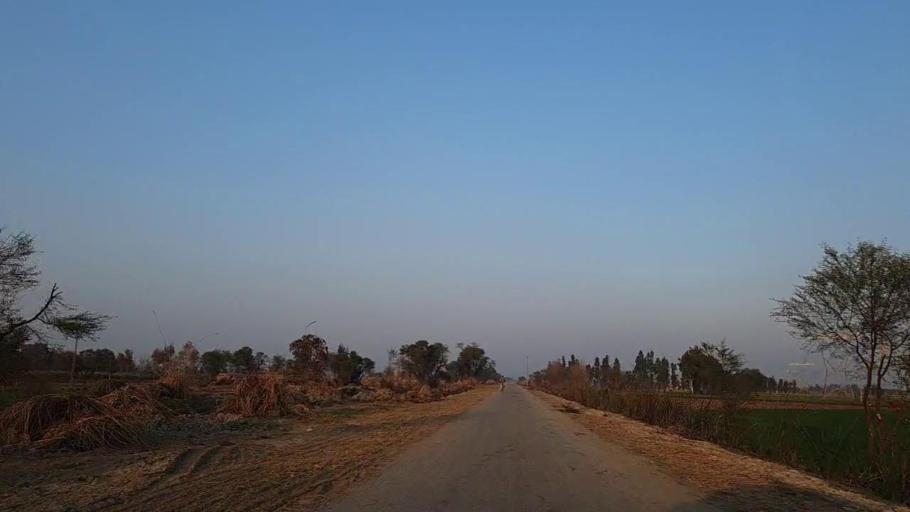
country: PK
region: Sindh
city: Naushahro Firoz
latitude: 26.7712
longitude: 68.0577
